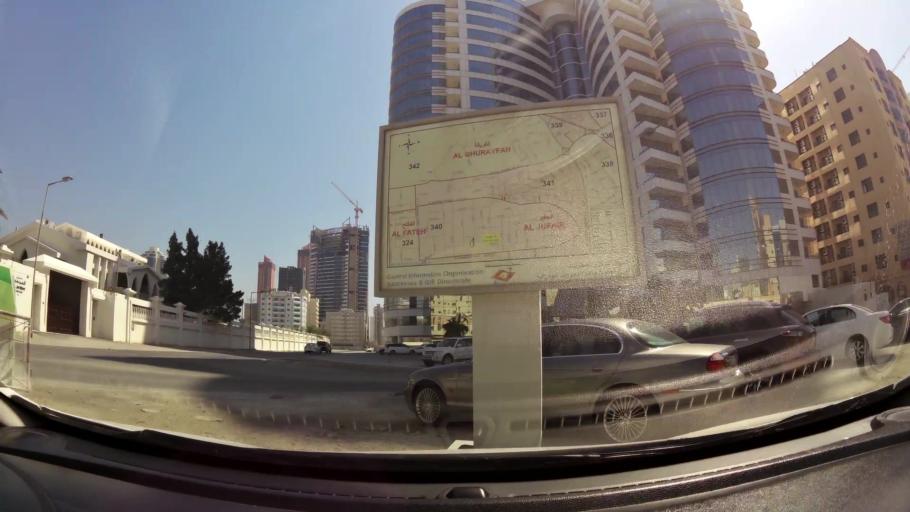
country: BH
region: Manama
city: Manama
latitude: 26.2152
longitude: 50.6053
